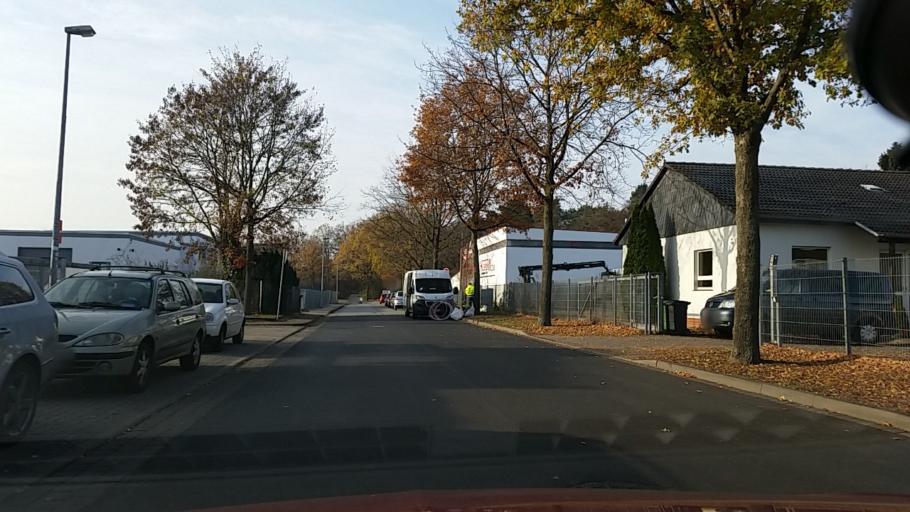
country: DE
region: Lower Saxony
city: Wolfsburg
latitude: 52.4295
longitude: 10.8217
